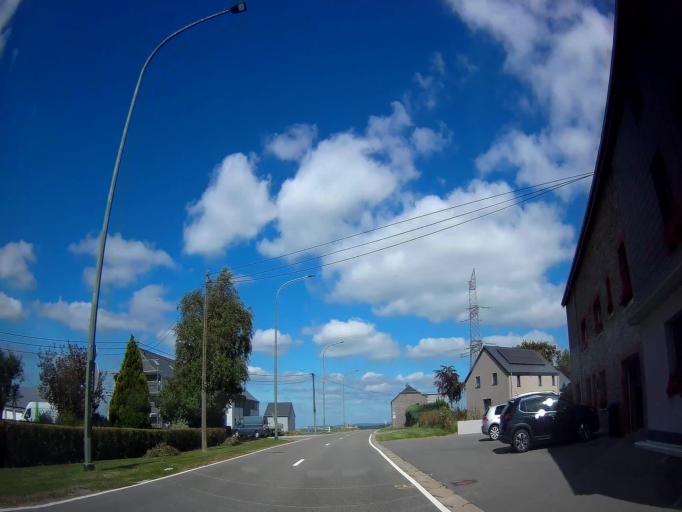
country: BE
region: Wallonia
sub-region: Province du Luxembourg
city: Bastogne
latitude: 50.0221
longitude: 5.7056
